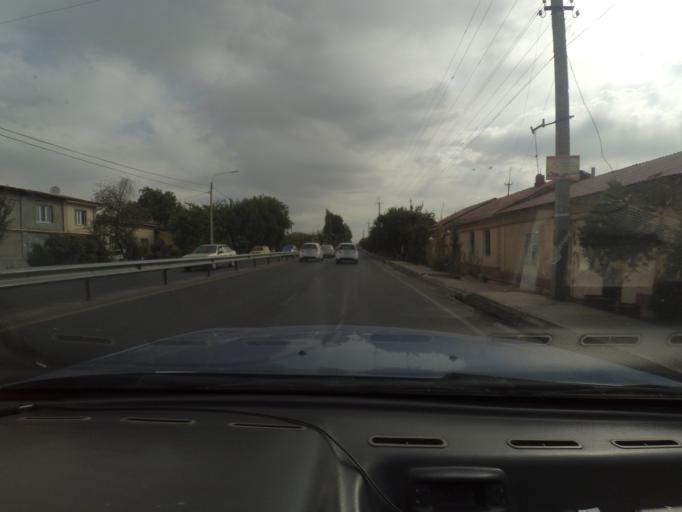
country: UZ
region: Toshkent
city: Qibray
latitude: 41.4001
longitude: 69.4898
